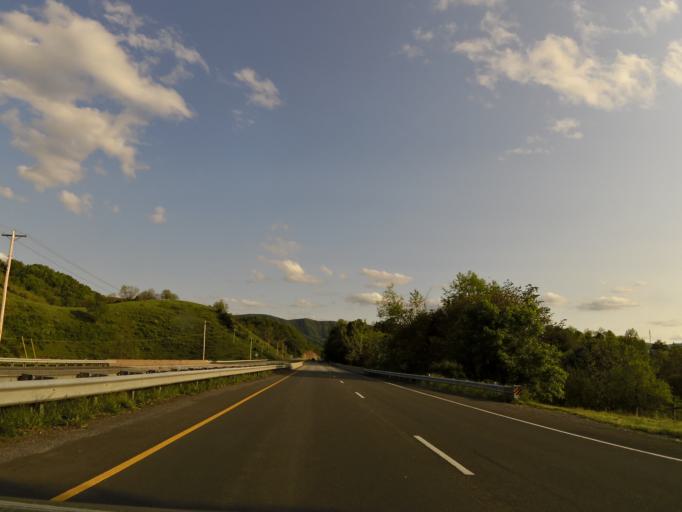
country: US
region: Virginia
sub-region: Tazewell County
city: Claypool Hill
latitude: 37.0302
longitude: -81.7982
